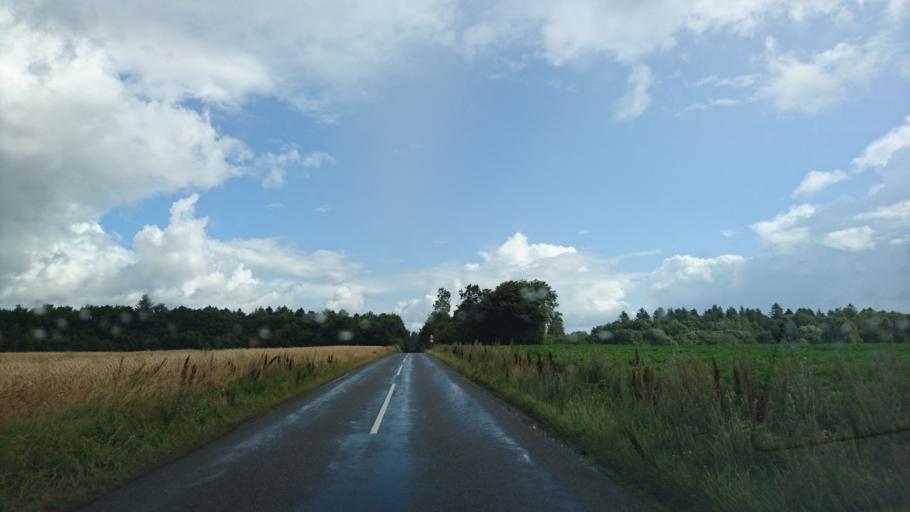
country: DK
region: North Denmark
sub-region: Hjorring Kommune
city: Sindal
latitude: 57.4696
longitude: 10.2553
